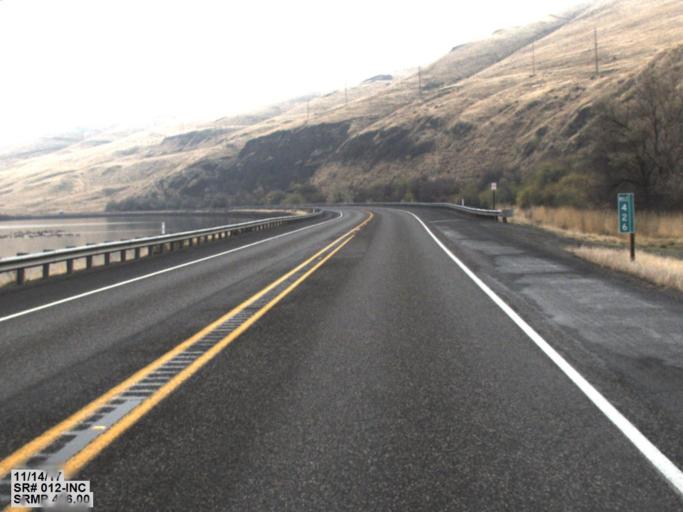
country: US
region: Washington
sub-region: Asotin County
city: Clarkston Heights-Vineland
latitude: 46.4128
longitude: -117.1950
